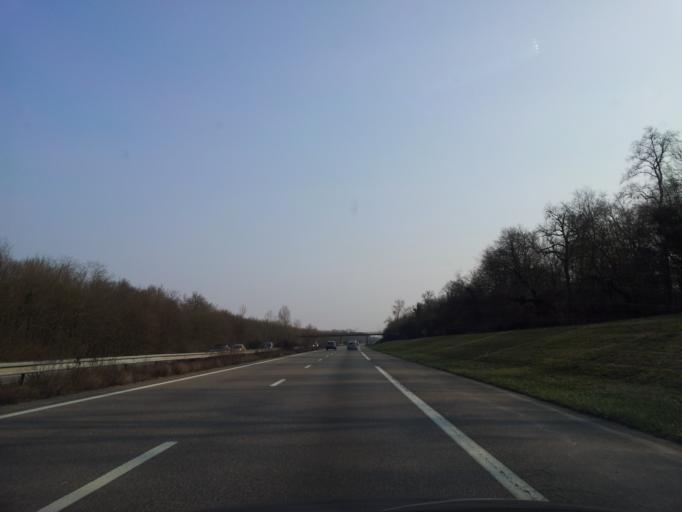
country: FR
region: Alsace
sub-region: Departement du Haut-Rhin
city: Bartenheim
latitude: 47.6548
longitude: 7.4885
